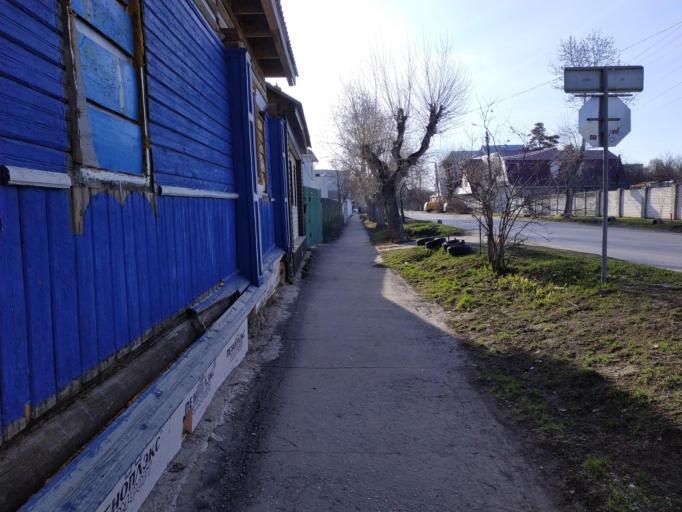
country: RU
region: Nizjnij Novgorod
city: Arzamas
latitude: 55.3944
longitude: 43.8144
